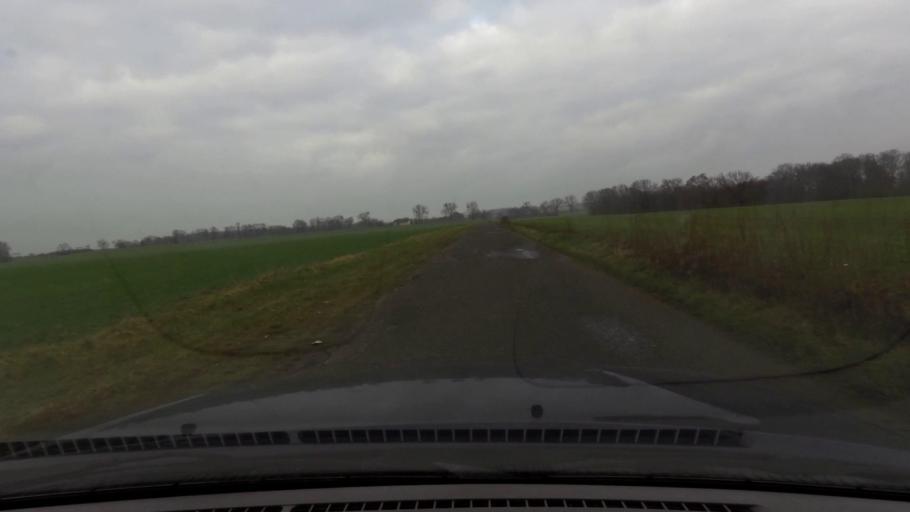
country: PL
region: West Pomeranian Voivodeship
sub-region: Powiat stargardzki
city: Stargard Szczecinski
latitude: 53.3431
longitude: 15.1259
